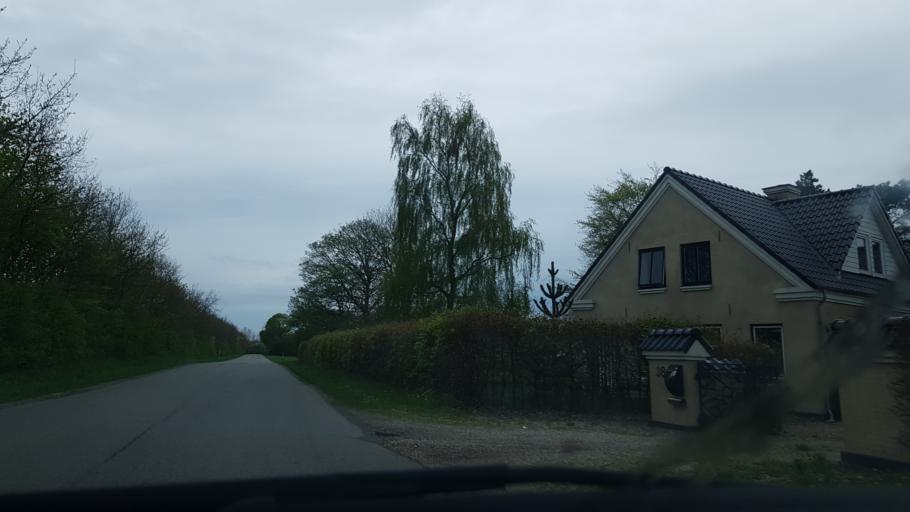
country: DK
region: South Denmark
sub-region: Kolding Kommune
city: Vamdrup
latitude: 55.4432
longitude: 9.3070
